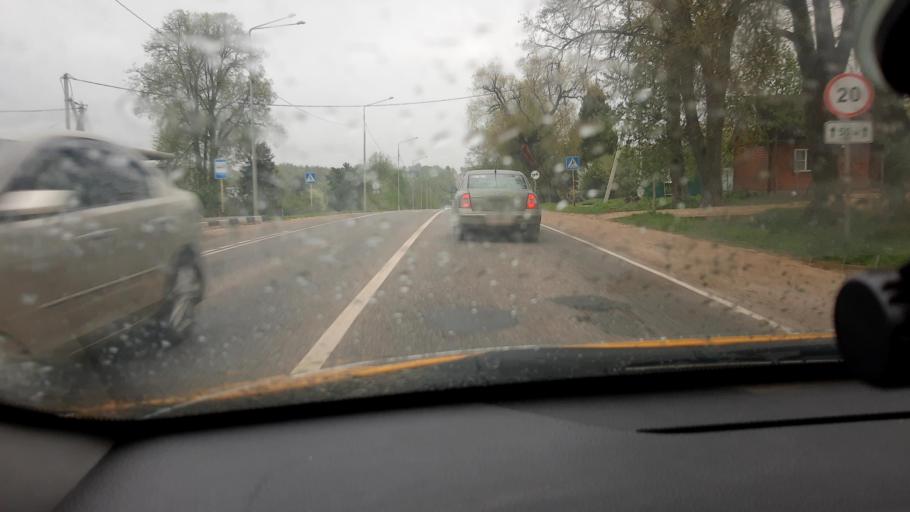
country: RU
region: Tula
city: Zaokskiy
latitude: 54.7607
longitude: 37.4373
